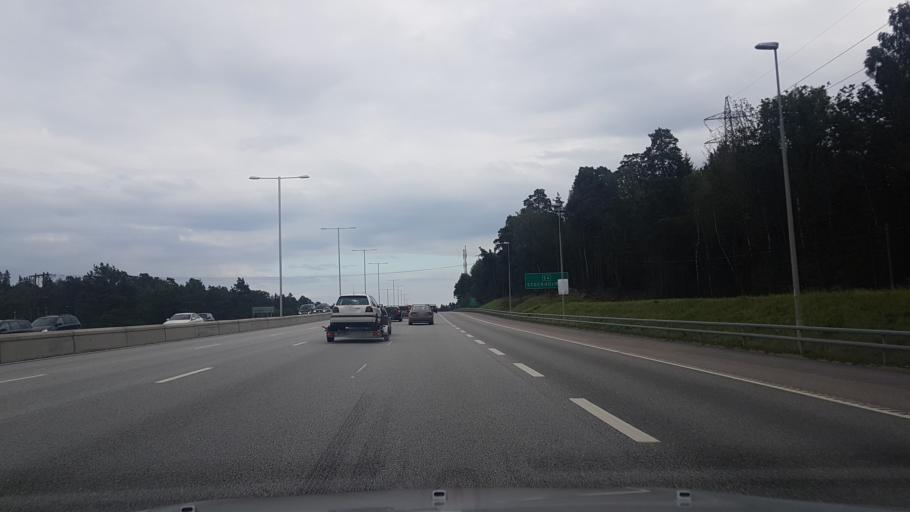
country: SE
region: Stockholm
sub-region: Solna Kommun
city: Rasunda
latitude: 59.3964
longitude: 17.9819
